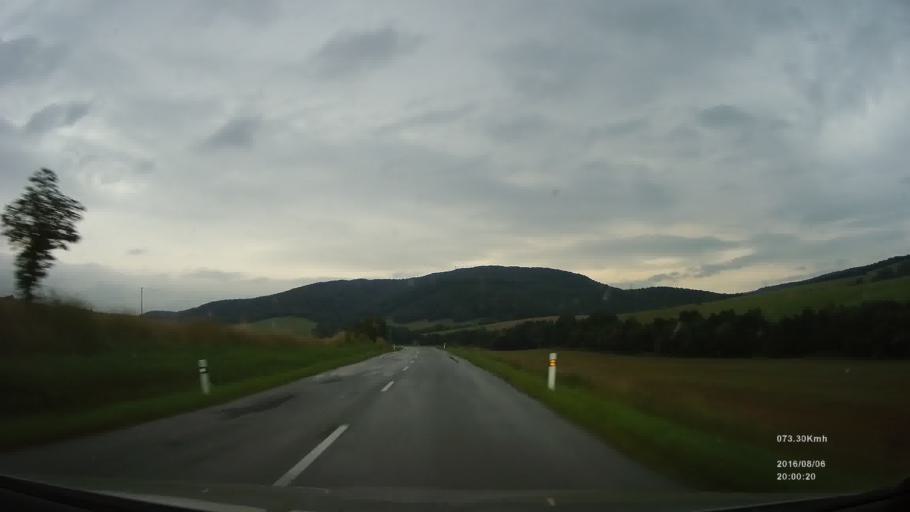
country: SK
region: Presovsky
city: Svidnik
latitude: 49.2535
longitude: 21.5813
